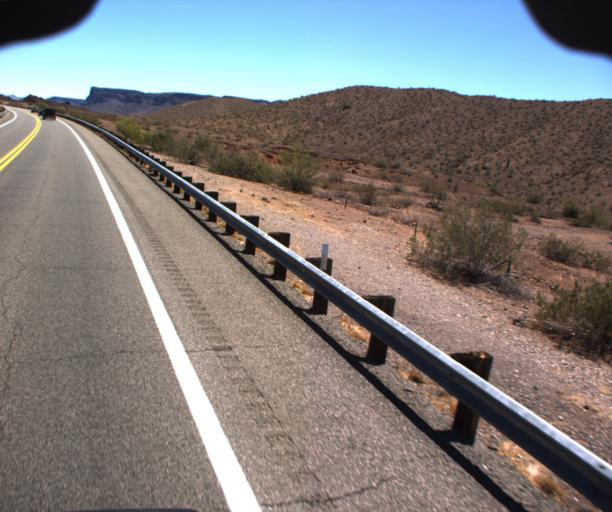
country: US
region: Arizona
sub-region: La Paz County
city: Cienega Springs
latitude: 34.3276
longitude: -114.1317
